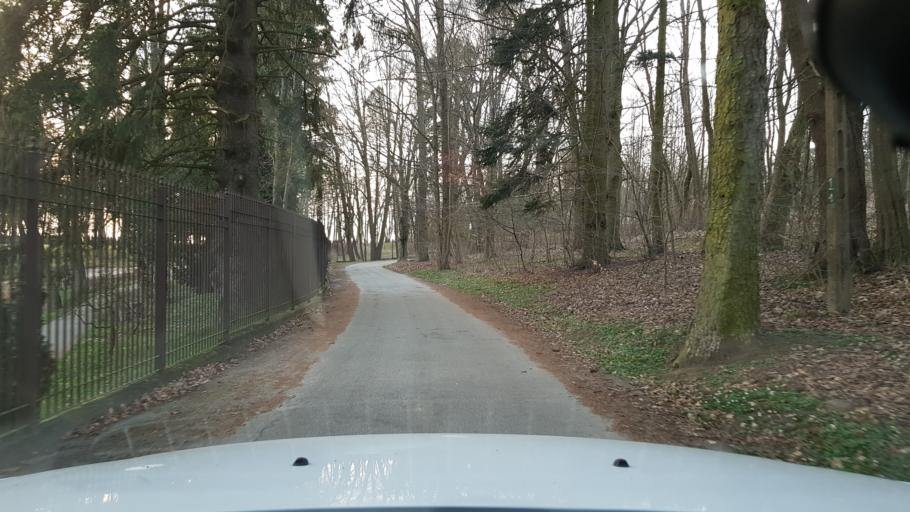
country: PL
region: West Pomeranian Voivodeship
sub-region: Koszalin
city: Koszalin
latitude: 54.1027
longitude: 16.1628
